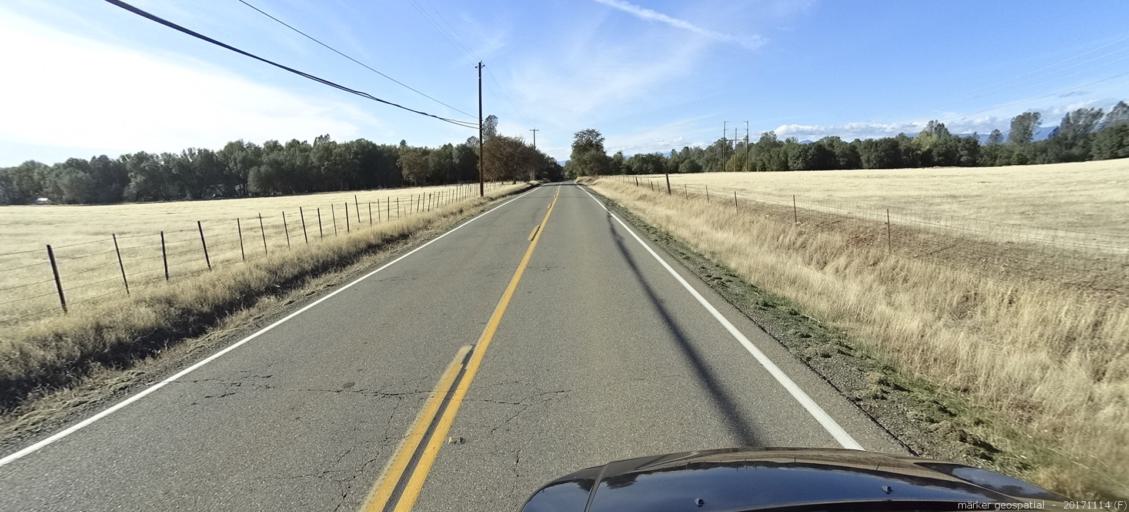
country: US
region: California
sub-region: Shasta County
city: Anderson
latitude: 40.3885
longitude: -122.4196
